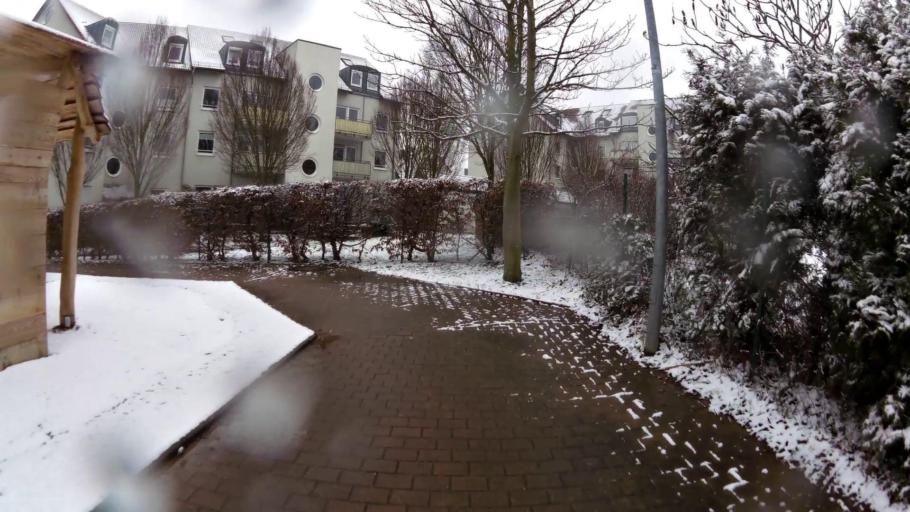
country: DE
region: Thuringia
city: Weimar
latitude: 50.9640
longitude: 11.3230
